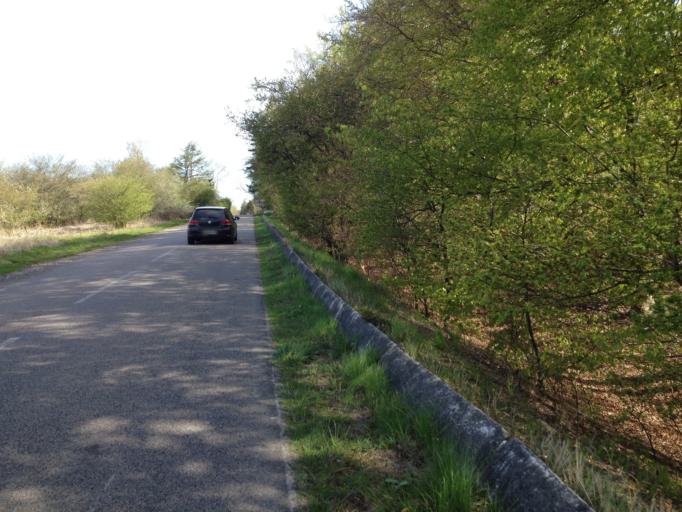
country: DK
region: Capital Region
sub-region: Halsnaes Kommune
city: Hundested
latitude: 55.9575
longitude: 11.9014
